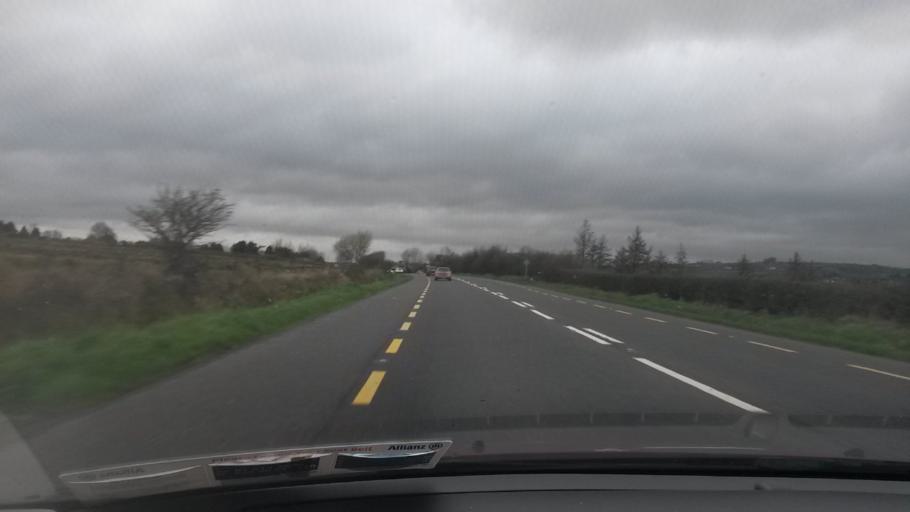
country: IE
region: Munster
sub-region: County Limerick
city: Abbeyfeale
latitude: 52.3845
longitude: -9.2290
